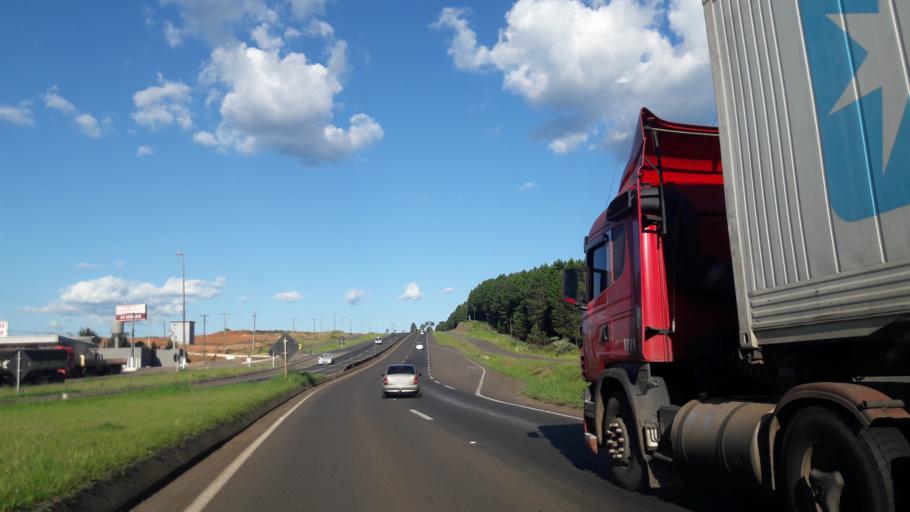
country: BR
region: Parana
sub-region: Guarapuava
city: Guarapuava
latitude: -25.3447
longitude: -51.4419
